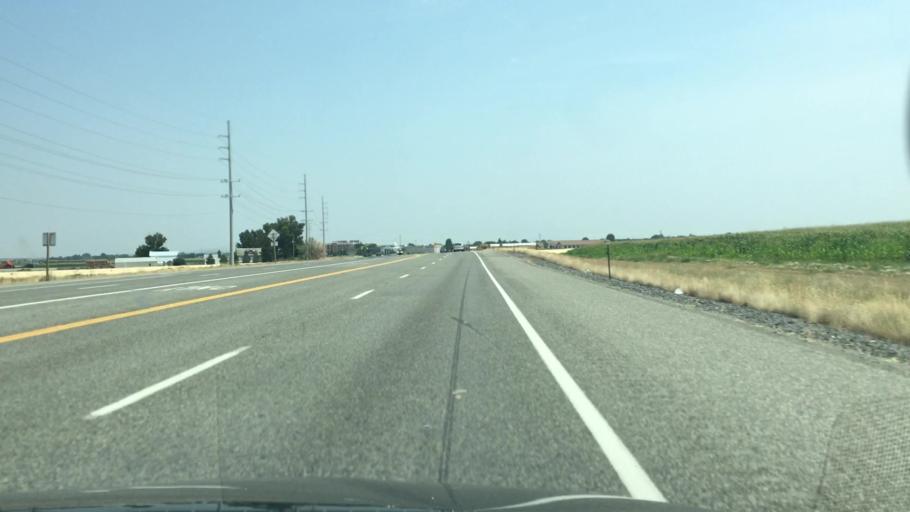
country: US
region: Idaho
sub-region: Twin Falls County
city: Twin Falls
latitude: 42.5926
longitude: -114.5155
